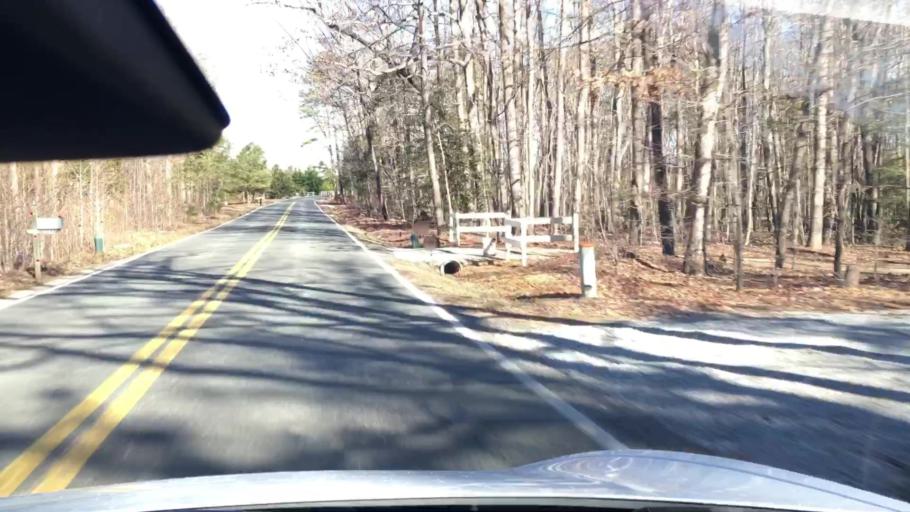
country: US
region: Virginia
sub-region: Powhatan County
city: Powhatan
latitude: 37.5462
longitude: -77.7935
